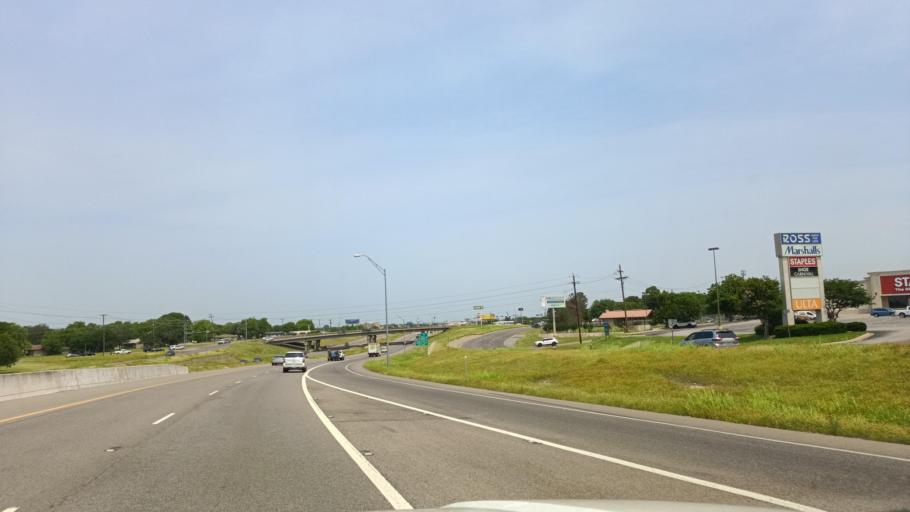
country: US
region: Texas
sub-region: Bell County
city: Temple
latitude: 31.0774
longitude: -97.3805
